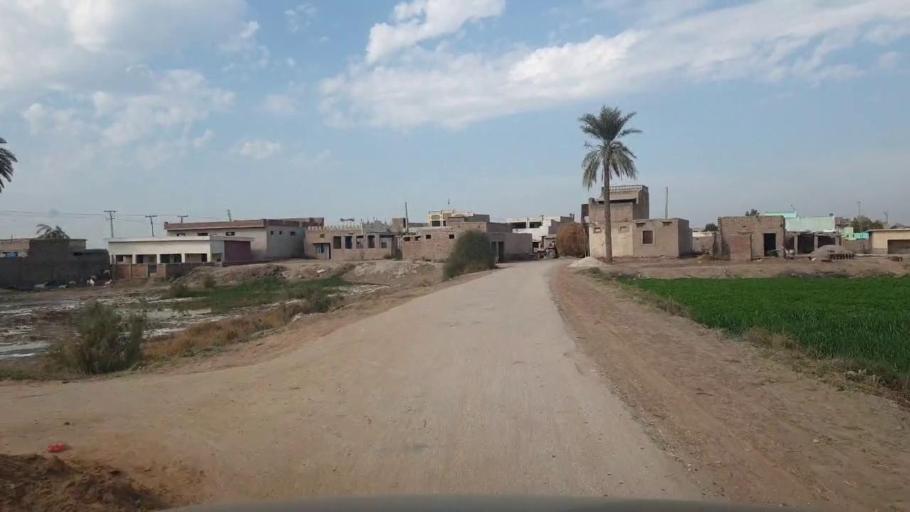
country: PK
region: Sindh
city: Sakrand
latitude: 26.0113
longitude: 68.4104
